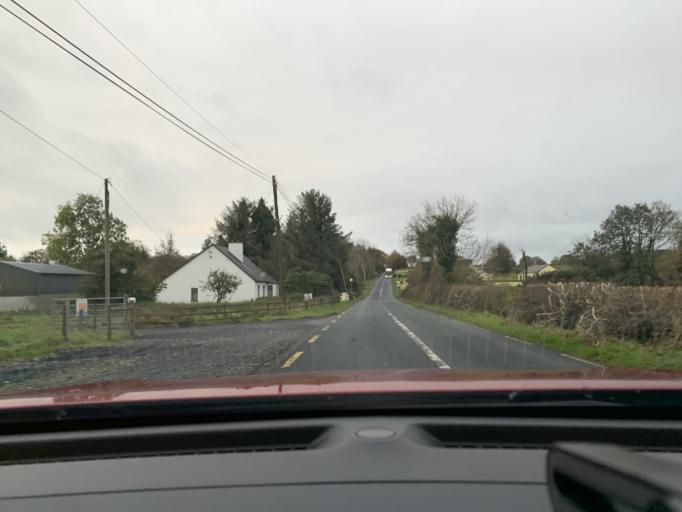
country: IE
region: Connaught
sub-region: Roscommon
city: Ballaghaderreen
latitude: 53.9792
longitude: -8.5352
